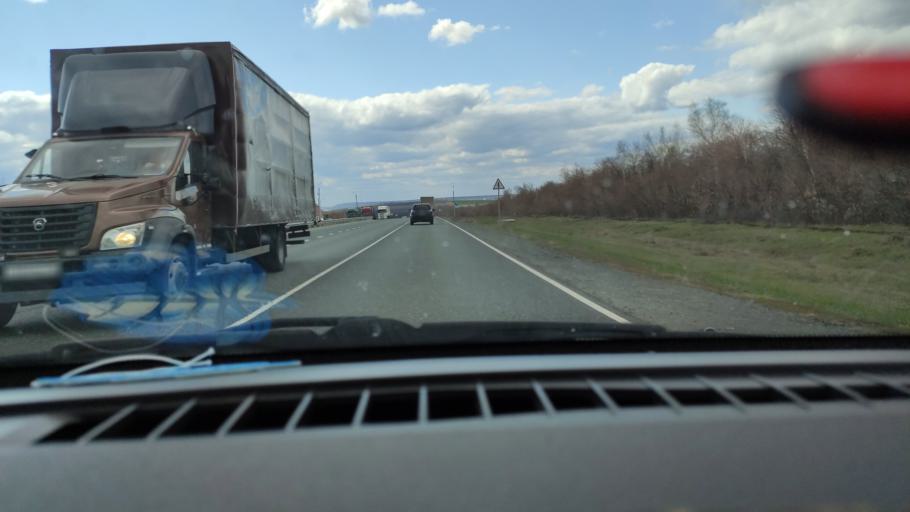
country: RU
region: Saratov
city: Balakovo
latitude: 52.1564
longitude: 47.8172
